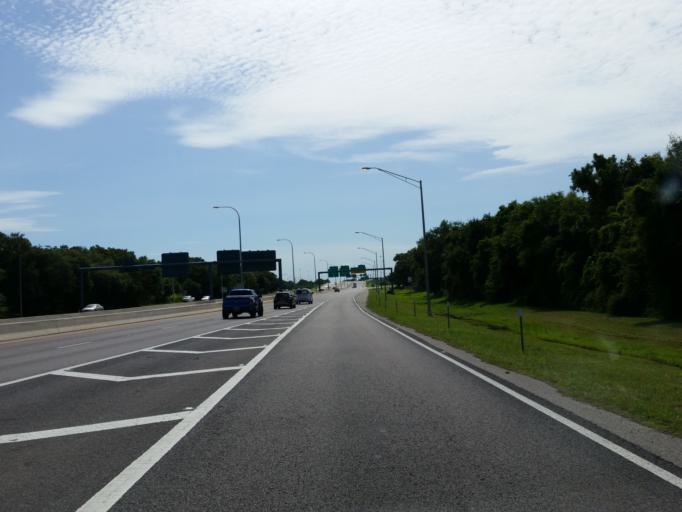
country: US
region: Florida
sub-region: Hillsborough County
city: Palm River-Clair Mel
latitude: 27.9297
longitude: -82.3477
